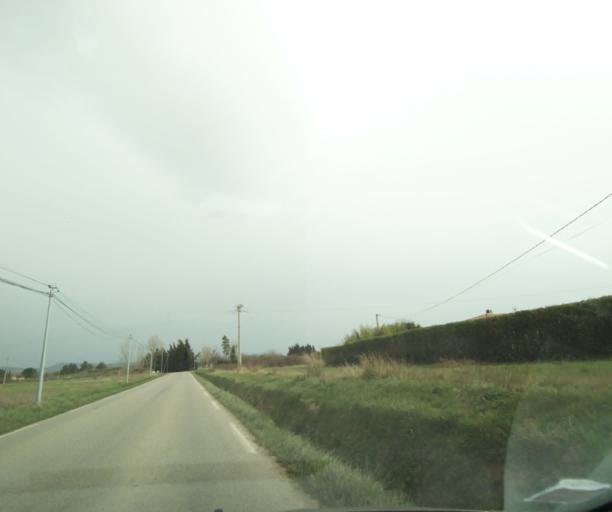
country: FR
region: Provence-Alpes-Cote d'Azur
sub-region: Departement des Bouches-du-Rhone
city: Trets
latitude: 43.4558
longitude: 5.6960
